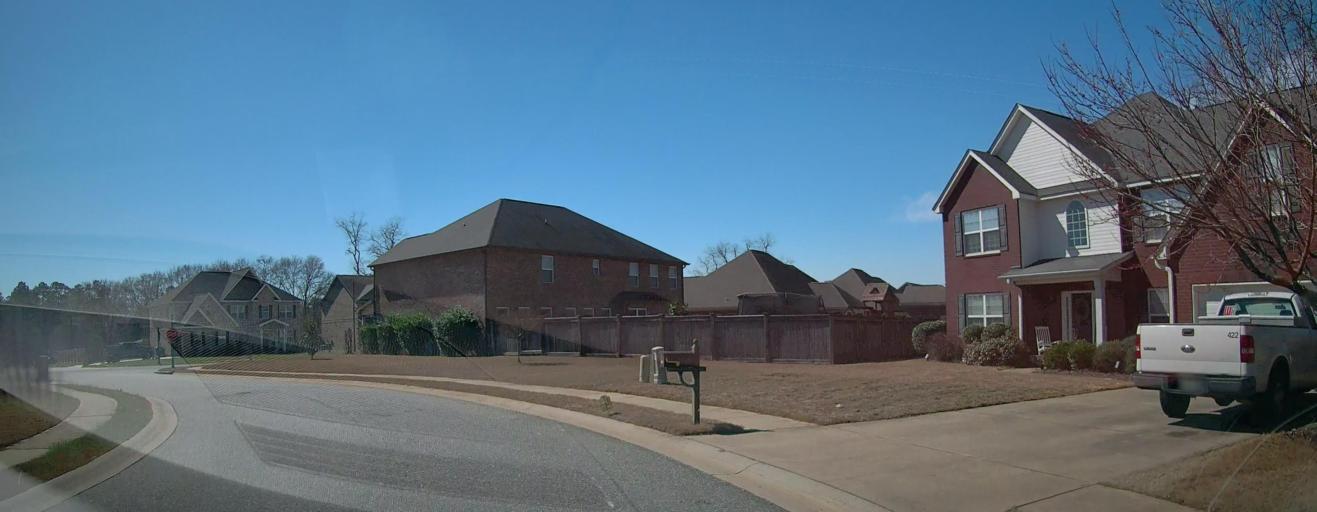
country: US
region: Georgia
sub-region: Houston County
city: Perry
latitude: 32.4956
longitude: -83.6580
